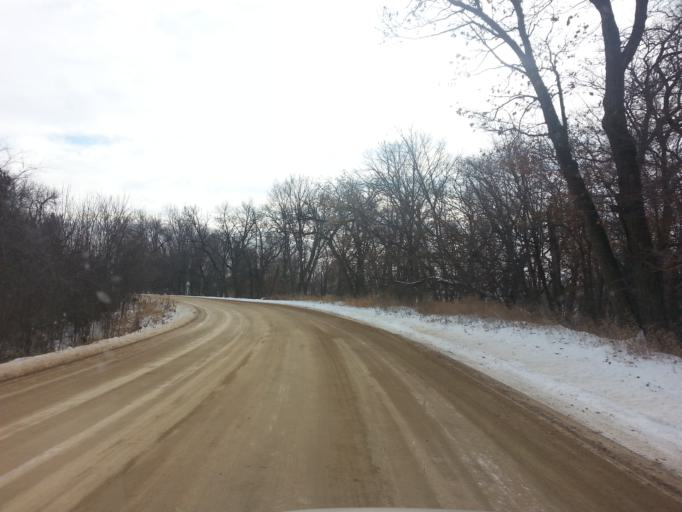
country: US
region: Minnesota
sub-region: Scott County
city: Prior Lake
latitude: 44.7221
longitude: -93.4798
